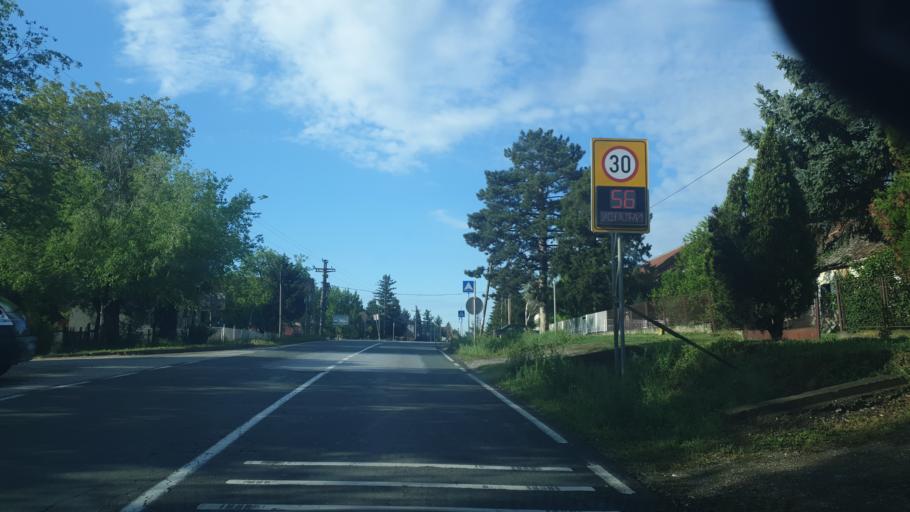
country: RS
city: Stubline
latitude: 44.5750
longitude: 20.1523
